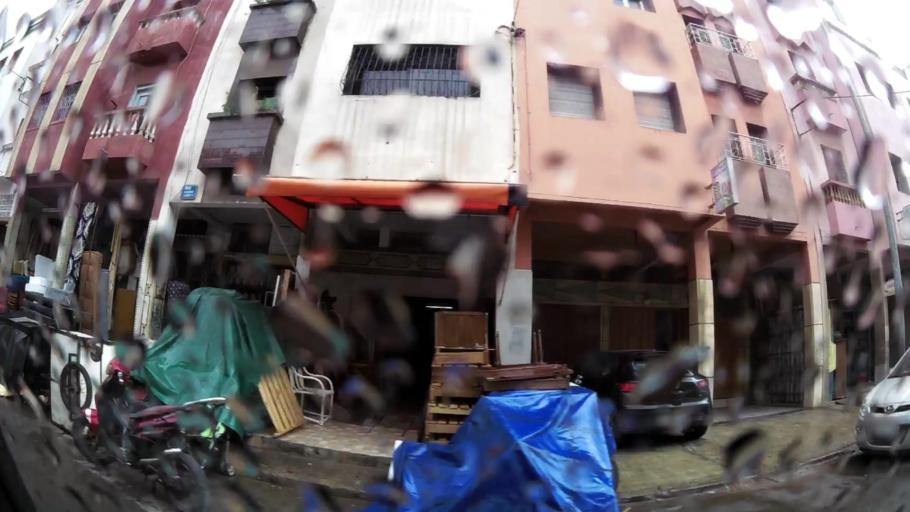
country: MA
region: Grand Casablanca
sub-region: Mediouna
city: Tit Mellil
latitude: 33.6160
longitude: -7.4931
